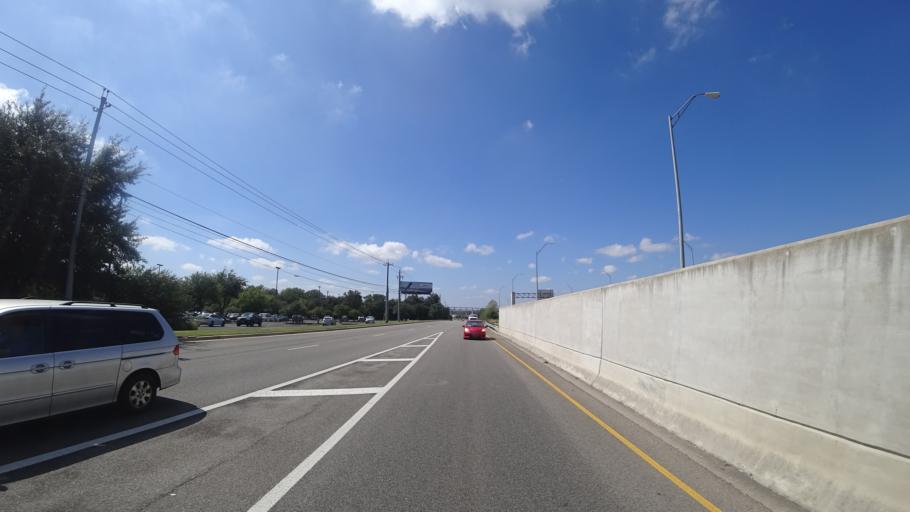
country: US
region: Texas
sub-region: Williamson County
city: Jollyville
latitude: 30.4738
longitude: -97.7758
